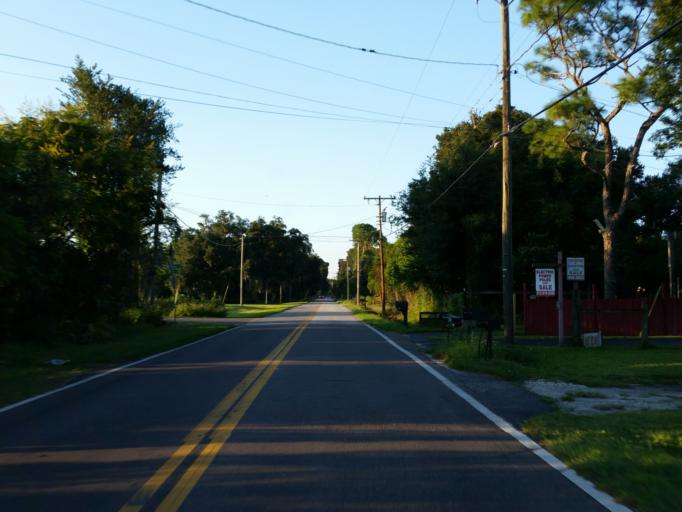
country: US
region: Florida
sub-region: Hillsborough County
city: Dover
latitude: 28.0265
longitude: -82.2447
